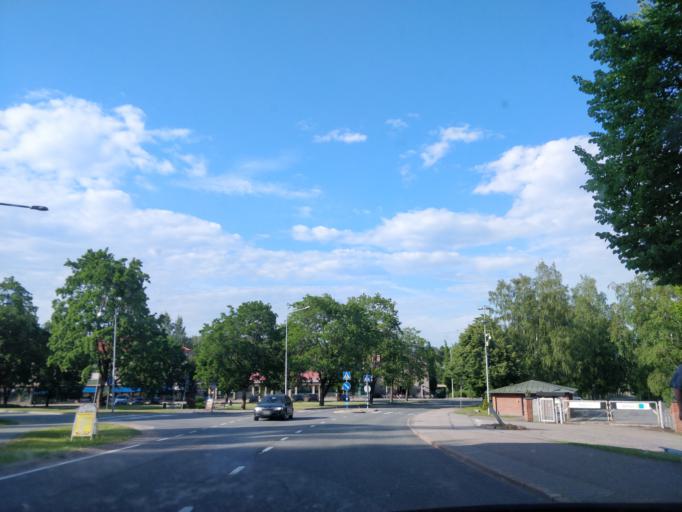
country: FI
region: Haeme
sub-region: Haemeenlinna
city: Tervakoski
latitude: 60.8143
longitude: 24.6256
